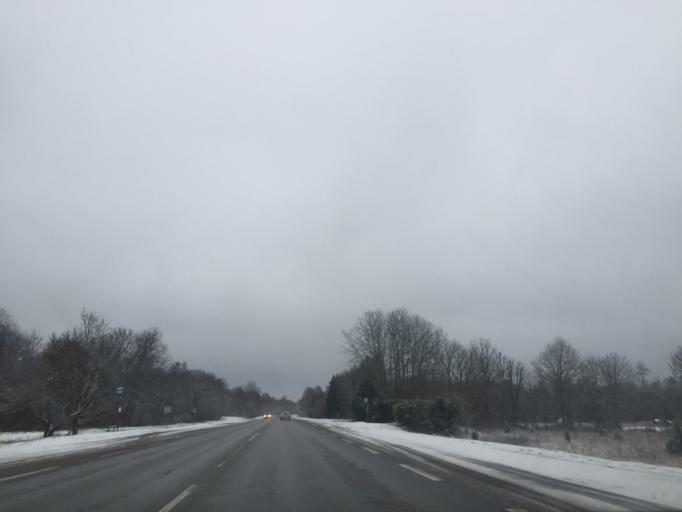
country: EE
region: Laeaene
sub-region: Lihula vald
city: Lihula
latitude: 58.6216
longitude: 23.6342
